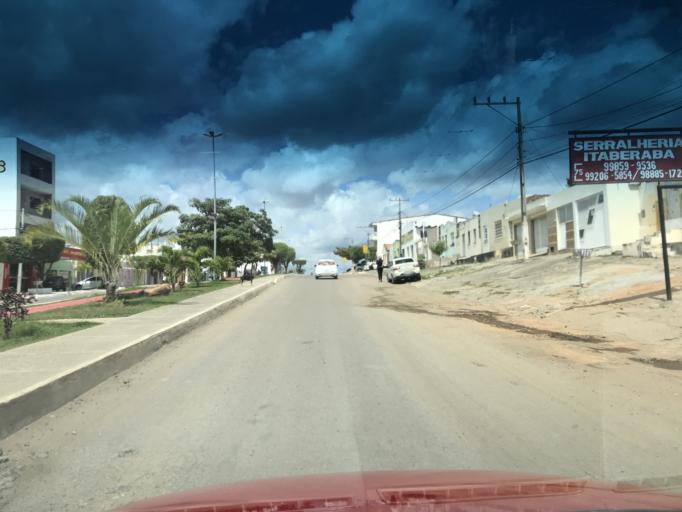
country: BR
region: Bahia
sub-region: Itaberaba
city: Itaberaba
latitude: -12.5244
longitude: -40.3065
